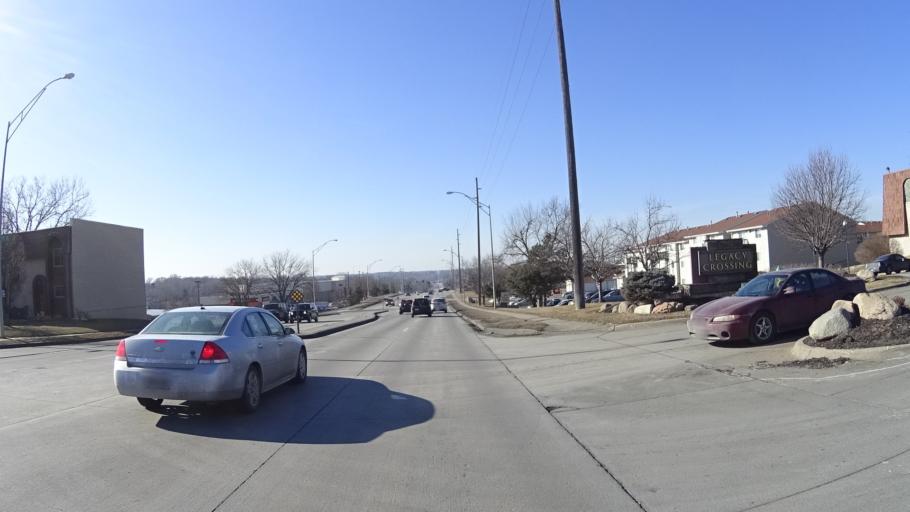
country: US
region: Nebraska
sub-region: Douglas County
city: Bennington
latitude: 41.3067
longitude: -96.0773
